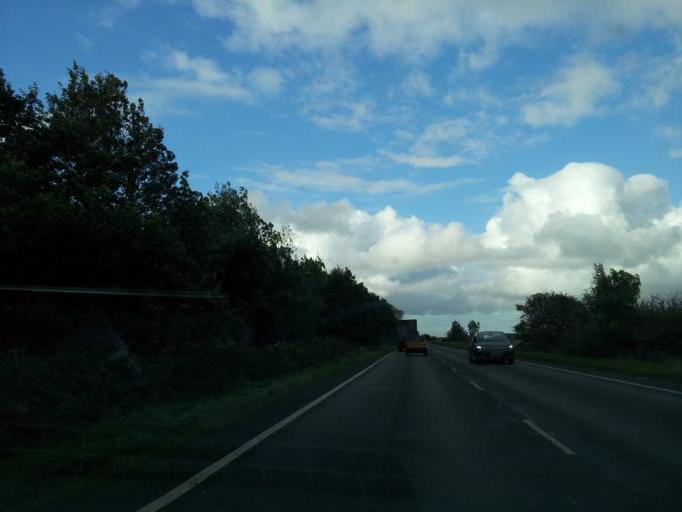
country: GB
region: England
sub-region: Norfolk
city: Terrington St Clement
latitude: 52.7468
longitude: 0.3218
